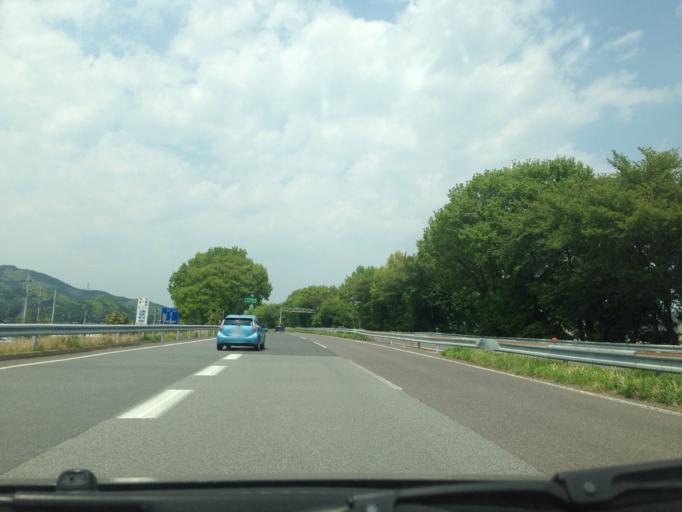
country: JP
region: Tochigi
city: Utsunomiya-shi
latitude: 36.6386
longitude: 139.8448
